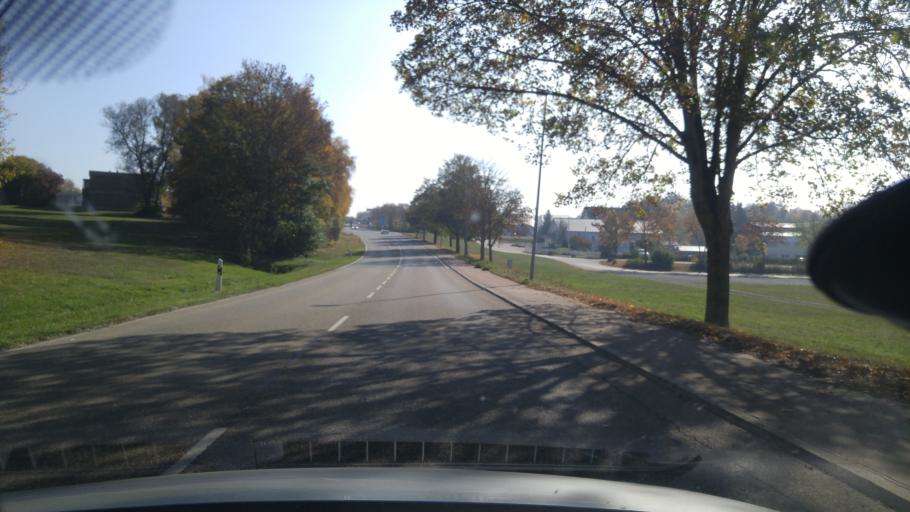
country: DE
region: Baden-Wuerttemberg
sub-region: Karlsruhe Region
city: Empfingen
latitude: 48.3878
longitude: 8.7185
